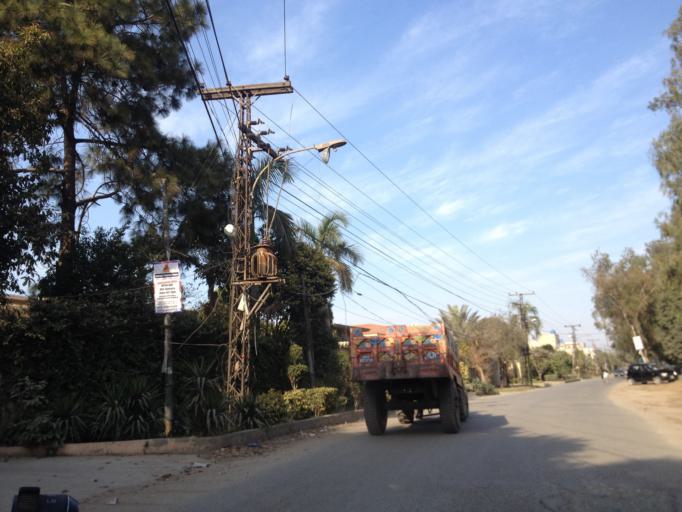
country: PK
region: Punjab
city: Lahore
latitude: 31.5062
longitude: 74.3186
